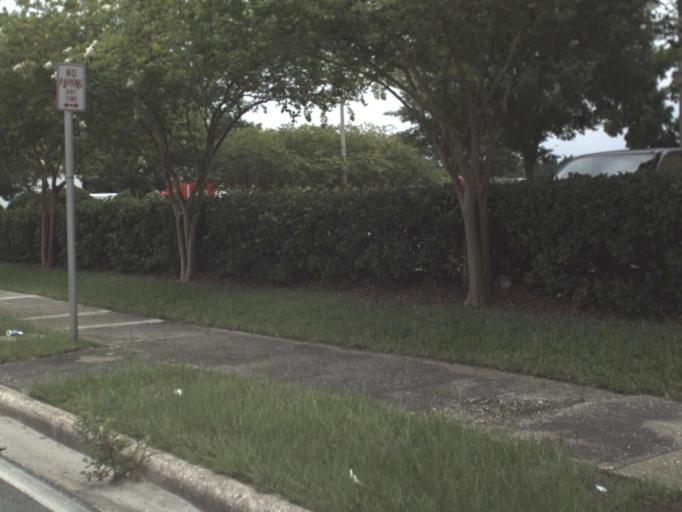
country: US
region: Florida
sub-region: Bradford County
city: Starke
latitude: 29.9440
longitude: -82.1123
